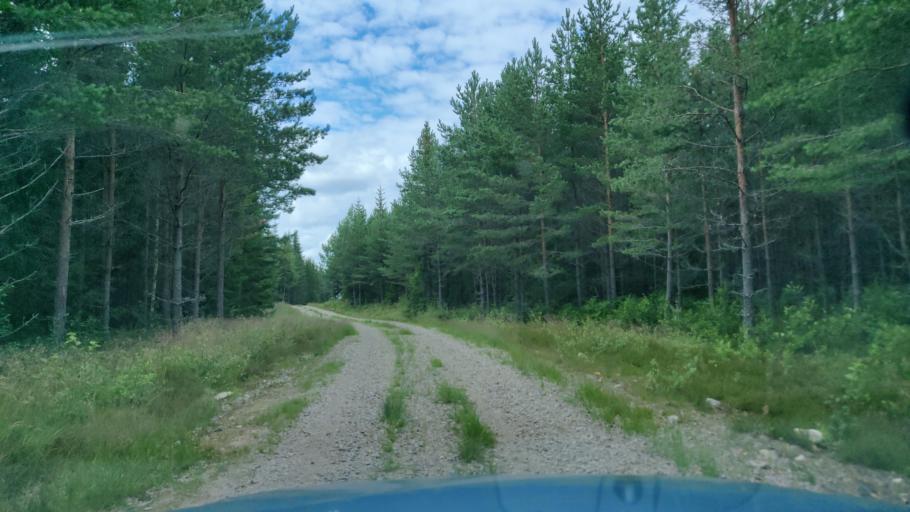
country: SE
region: Vaermland
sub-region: Hagfors Kommun
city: Hagfors
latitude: 59.9651
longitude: 13.5860
